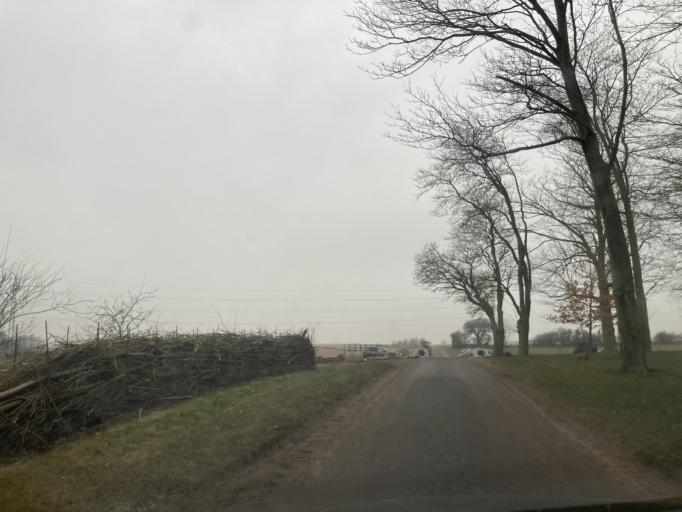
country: DK
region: Zealand
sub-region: Vordingborg Kommune
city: Neder Vindinge
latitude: 55.1545
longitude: 11.9063
